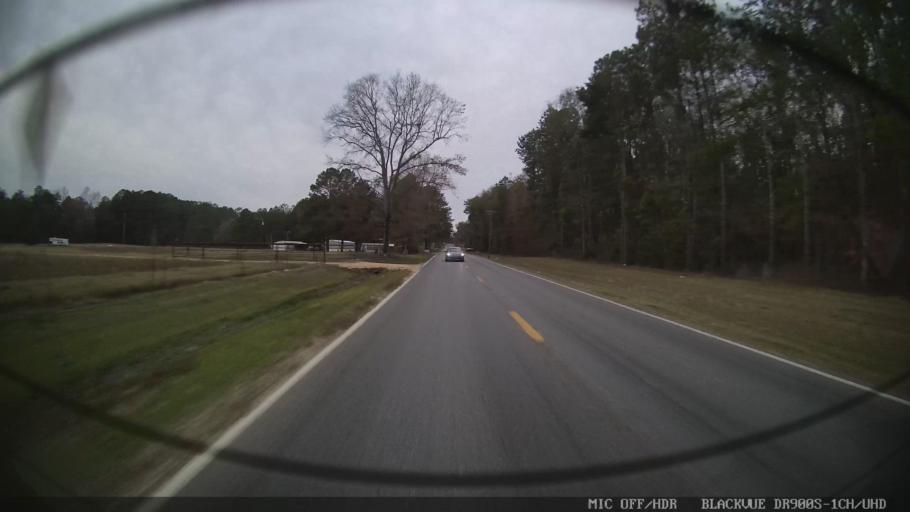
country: US
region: Mississippi
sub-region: Clarke County
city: Quitman
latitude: 32.0289
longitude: -88.8082
